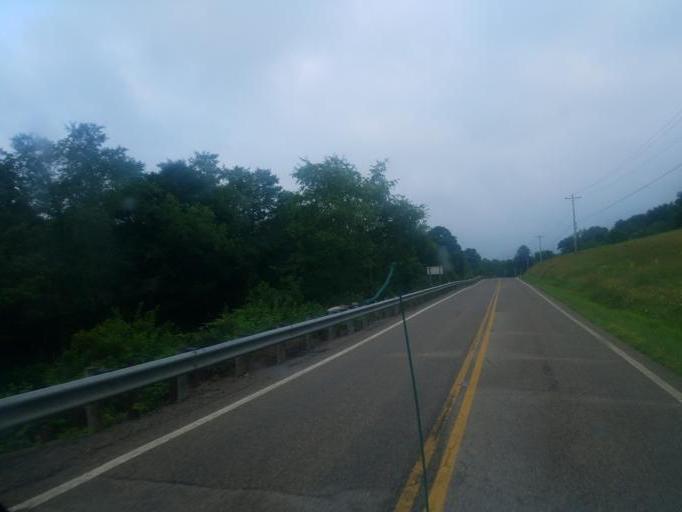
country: US
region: Ohio
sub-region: Columbiana County
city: Salineville
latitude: 40.5757
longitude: -80.9375
